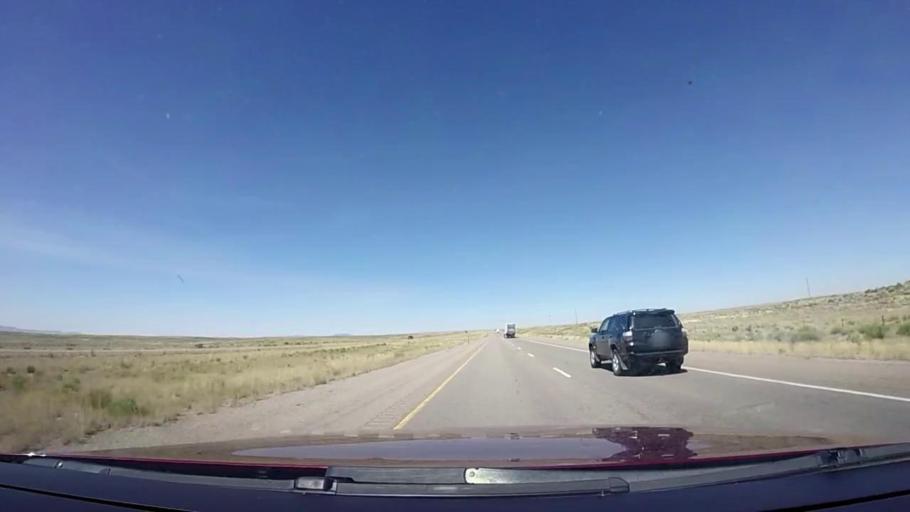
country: US
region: Wyoming
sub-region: Sweetwater County
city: Rock Springs
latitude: 41.6374
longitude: -108.4408
